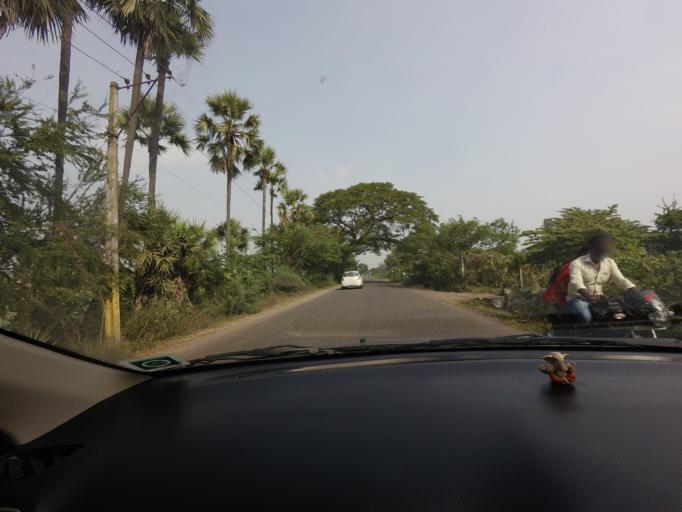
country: IN
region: Andhra Pradesh
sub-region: Krishna
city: Kankipadu
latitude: 16.4531
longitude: 80.7740
